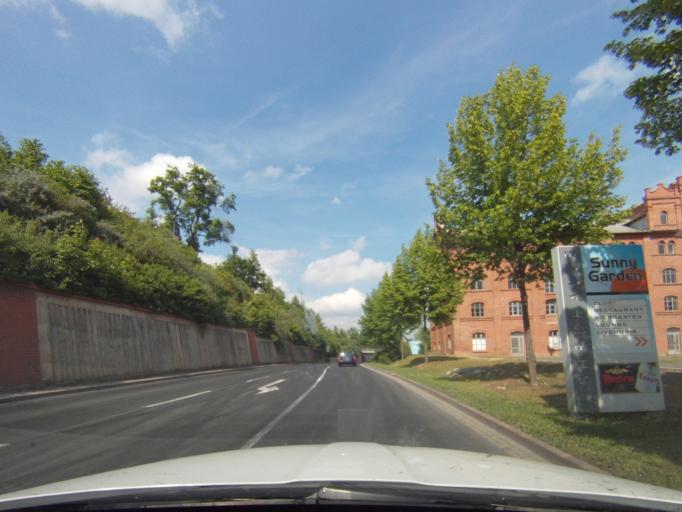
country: DE
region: Thuringia
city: Possneck
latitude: 50.6987
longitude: 11.5990
